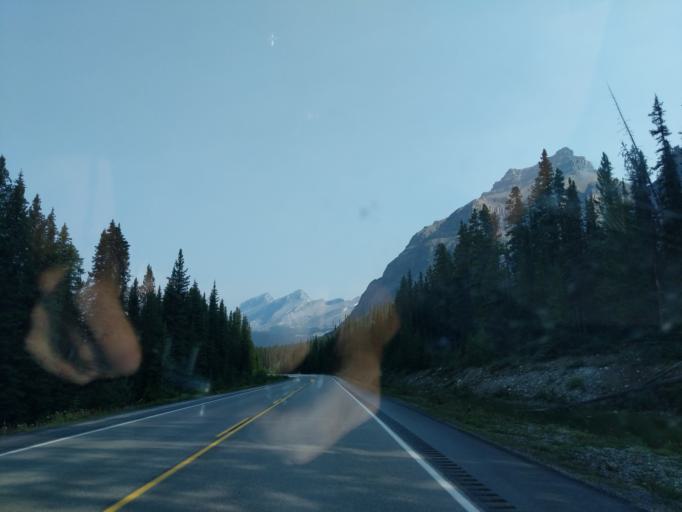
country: CA
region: Alberta
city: Lake Louise
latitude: 51.6168
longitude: -116.3160
